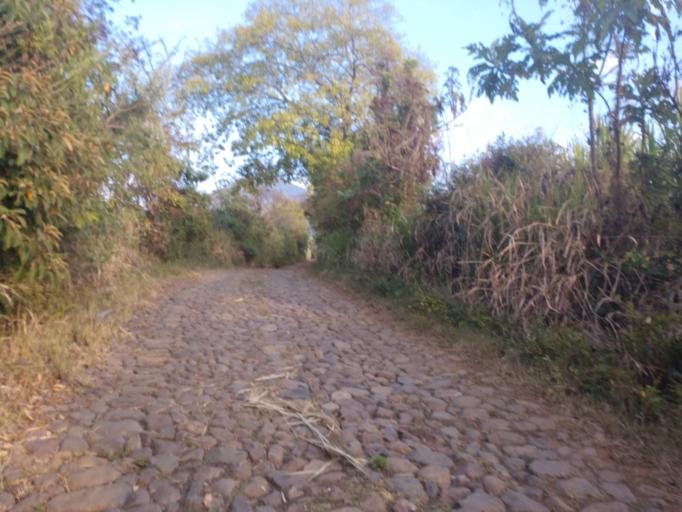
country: MX
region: Nayarit
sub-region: Tepic
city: La Corregidora
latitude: 21.4569
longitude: -104.7946
